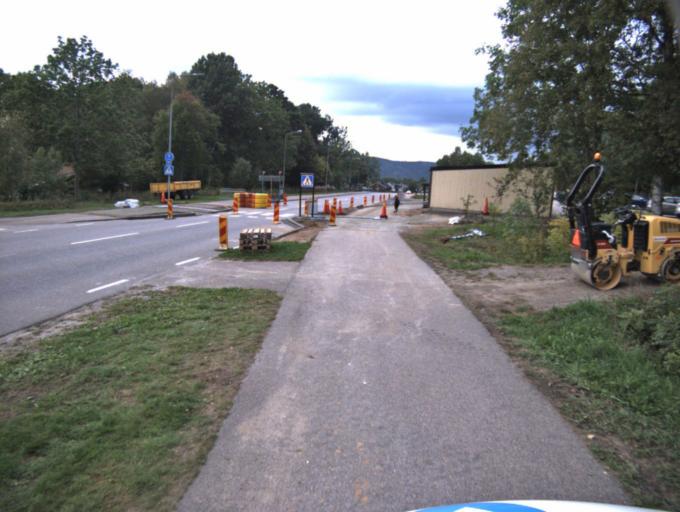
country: SE
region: Vaestra Goetaland
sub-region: Ulricehamns Kommun
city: Ulricehamn
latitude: 57.7927
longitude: 13.4253
